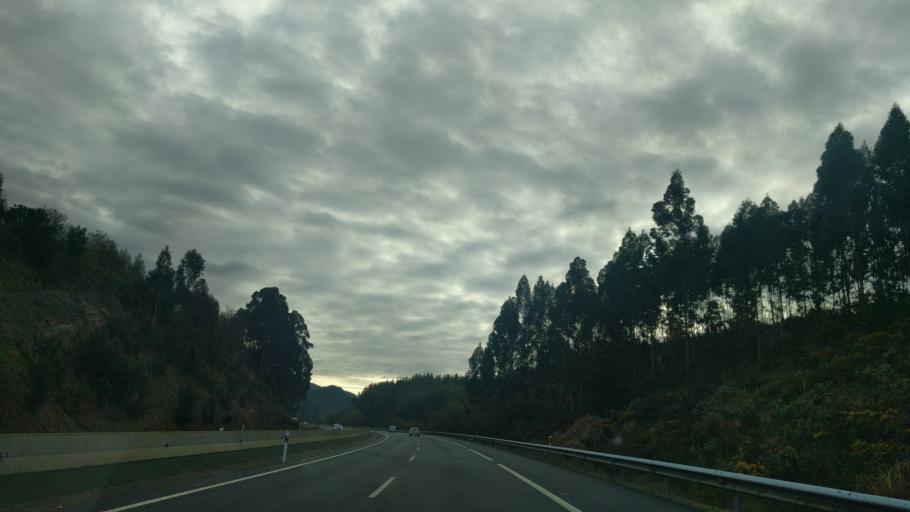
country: ES
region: Cantabria
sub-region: Provincia de Cantabria
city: Liendo
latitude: 43.3902
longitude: -3.3934
